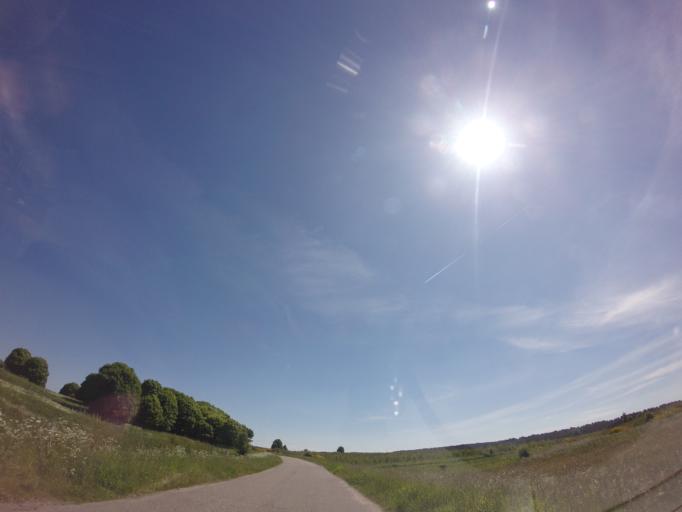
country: PL
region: West Pomeranian Voivodeship
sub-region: Powiat choszczenski
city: Recz
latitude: 53.3096
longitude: 15.6420
